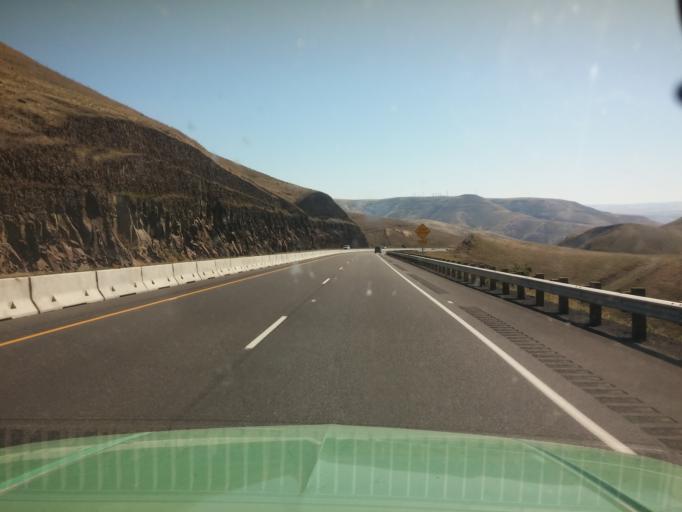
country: US
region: Idaho
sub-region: Nez Perce County
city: Lewiston
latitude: 46.4610
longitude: -116.9723
